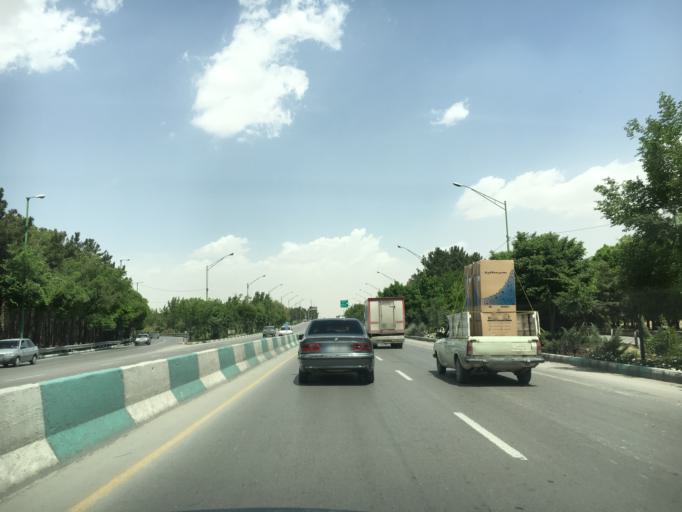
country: IR
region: Isfahan
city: Isfahan
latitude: 32.6952
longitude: 51.7344
